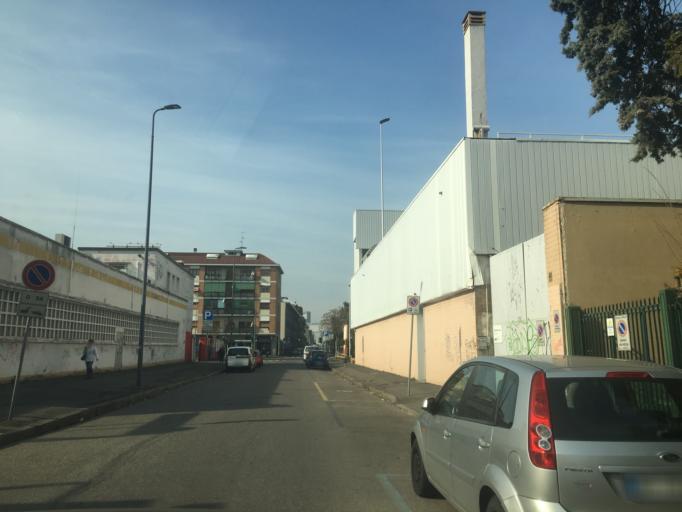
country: IT
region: Lombardy
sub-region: Citta metropolitana di Milano
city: Sesto San Giovanni
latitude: 45.5202
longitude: 9.2284
